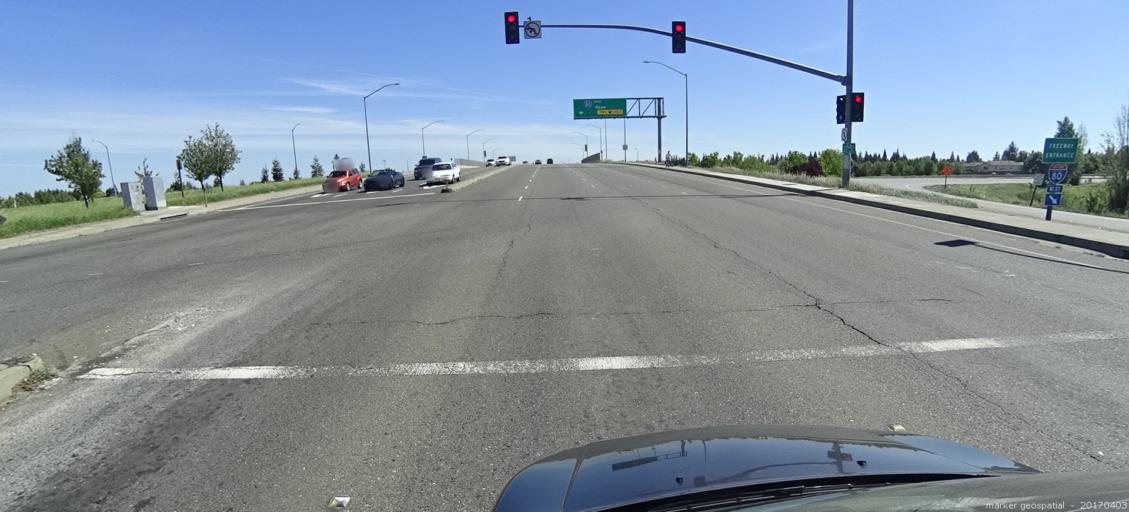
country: US
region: California
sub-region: Sacramento County
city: Sacramento
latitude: 38.6352
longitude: -121.5017
